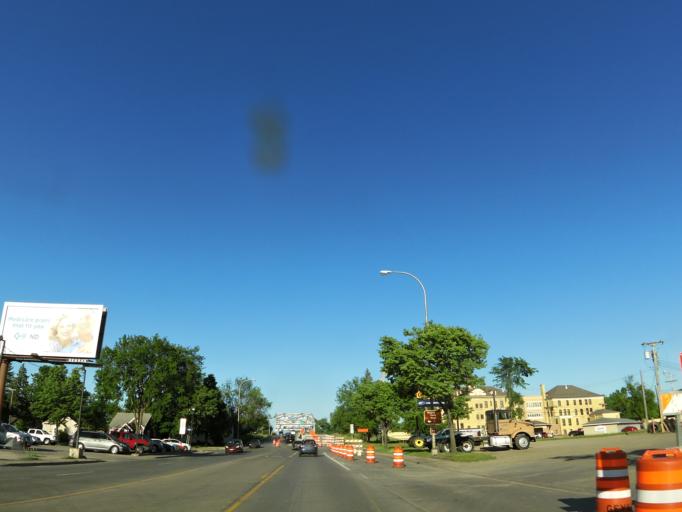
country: US
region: North Dakota
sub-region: Grand Forks County
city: Grand Forks
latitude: 47.9331
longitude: -97.0423
